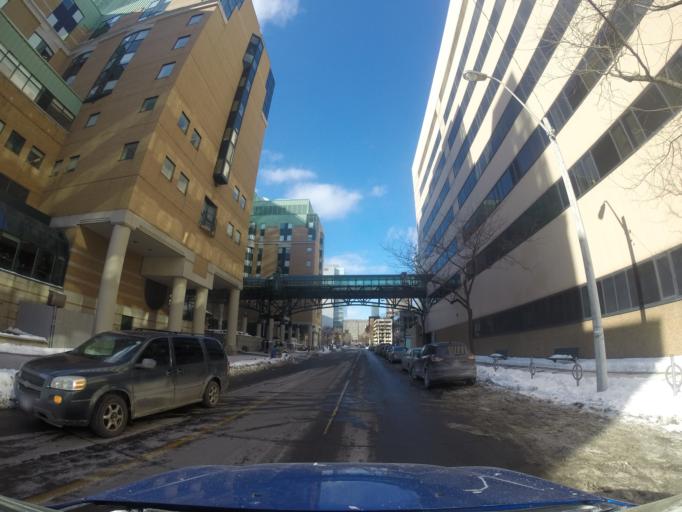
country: CA
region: Ontario
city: Toronto
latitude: 43.6571
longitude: -79.3858
